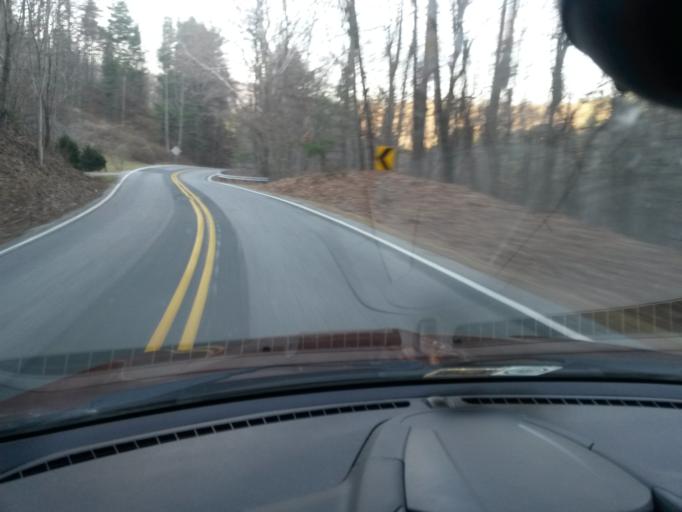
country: US
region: Virginia
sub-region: City of Buena Vista
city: Buena Vista
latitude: 37.7411
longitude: -79.2582
